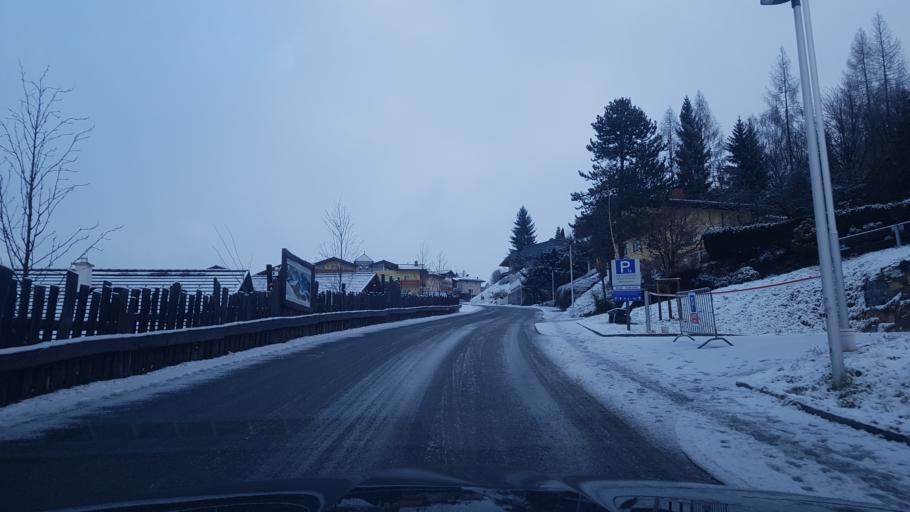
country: AT
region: Salzburg
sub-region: Politischer Bezirk Sankt Johann im Pongau
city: Sankt Johann im Pongau
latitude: 47.3257
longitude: 13.1996
